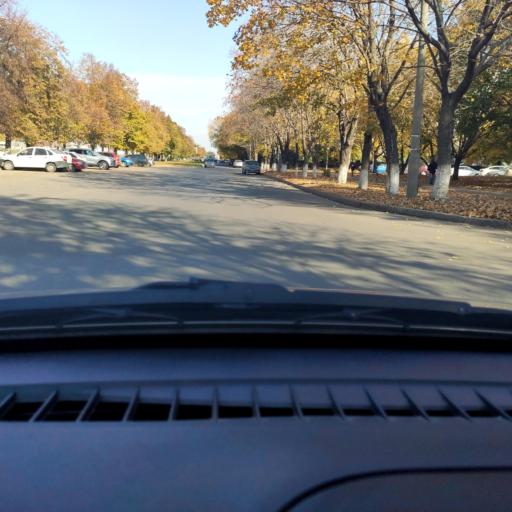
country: RU
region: Samara
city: Tol'yatti
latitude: 53.5338
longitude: 49.2630
